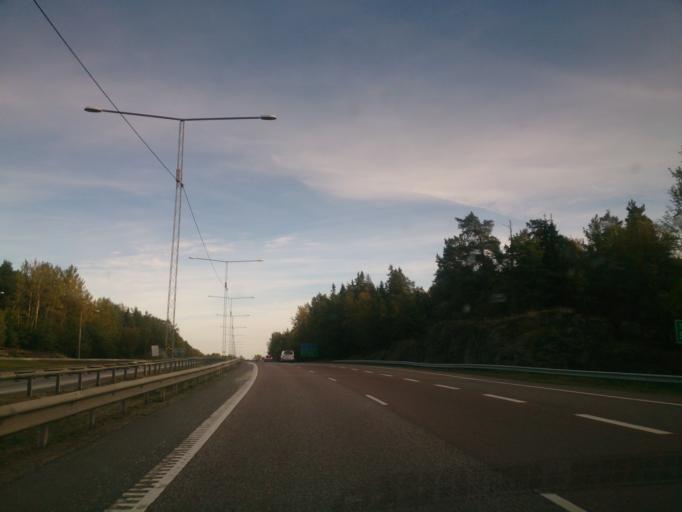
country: SE
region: Stockholm
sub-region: Nacka Kommun
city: Alta
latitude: 59.2502
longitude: 18.1717
